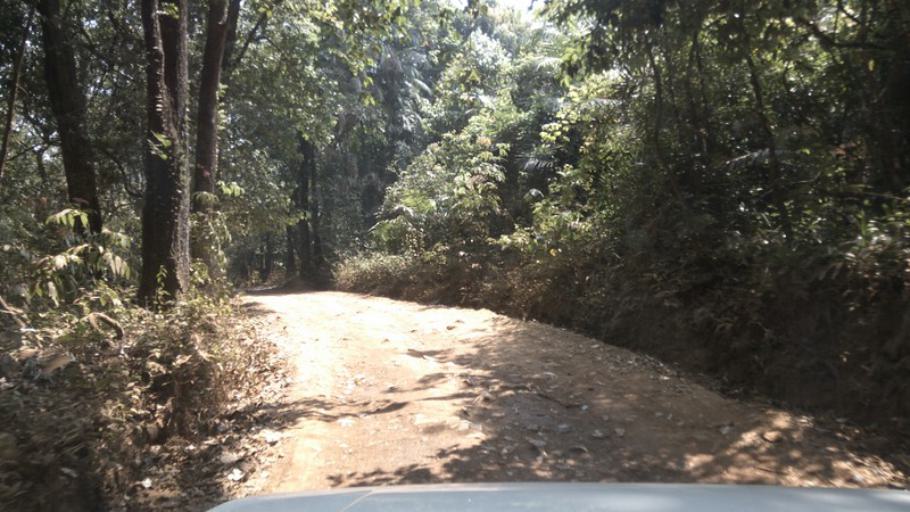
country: IN
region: Goa
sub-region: South Goa
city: Sanguem
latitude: 15.3143
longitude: 74.2932
